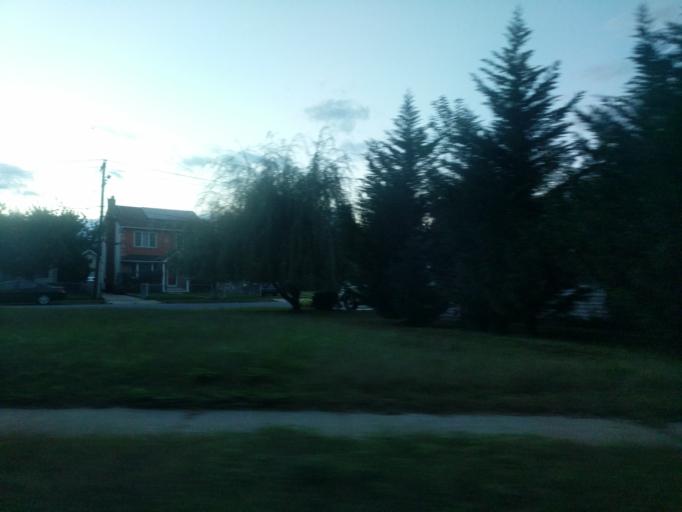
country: US
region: New York
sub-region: Nassau County
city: Garden City South
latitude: 40.6998
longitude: -73.6646
